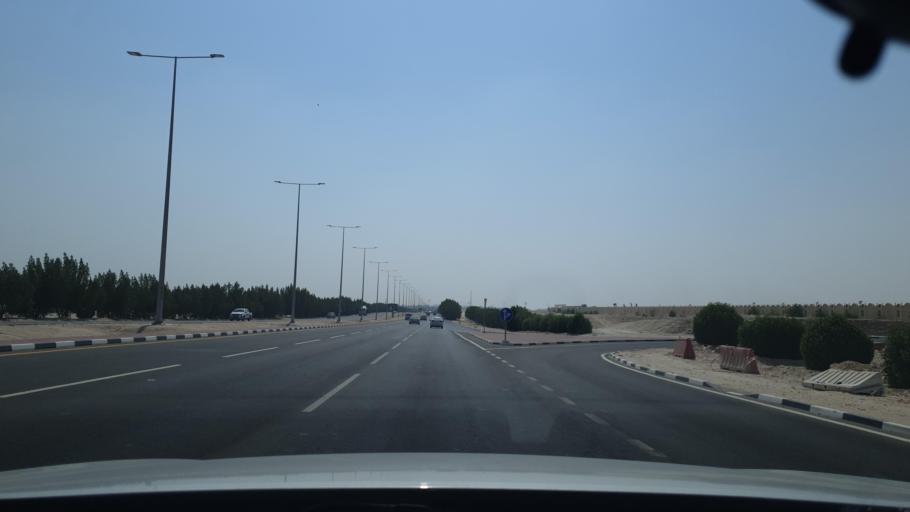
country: QA
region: Al Khawr
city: Al Khawr
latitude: 25.7077
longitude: 51.5050
